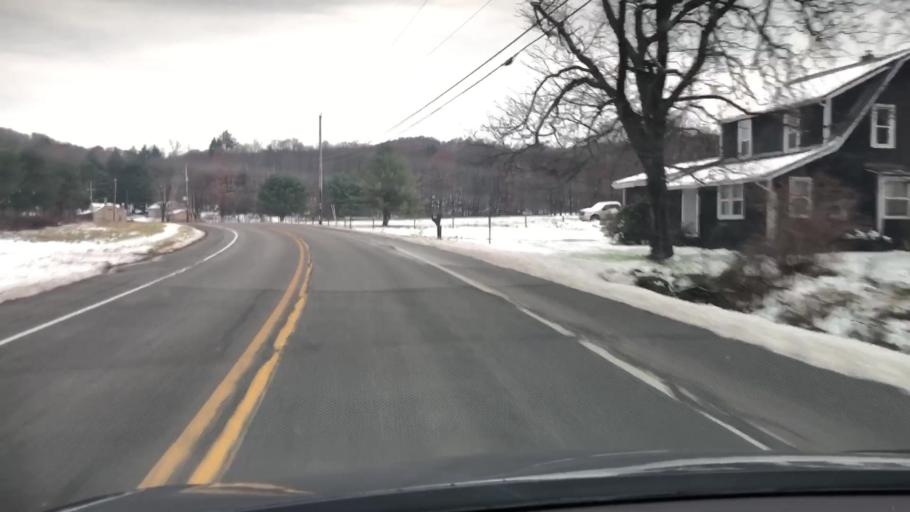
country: US
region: Pennsylvania
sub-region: Jefferson County
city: Brookville
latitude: 41.1365
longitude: -79.1464
